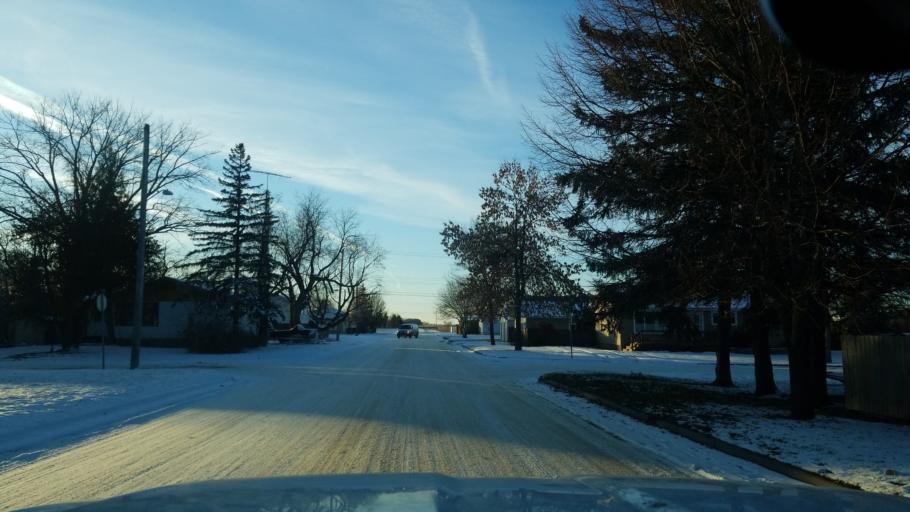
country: CA
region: Manitoba
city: Portage la Prairie
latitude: 49.9796
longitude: -98.3015
